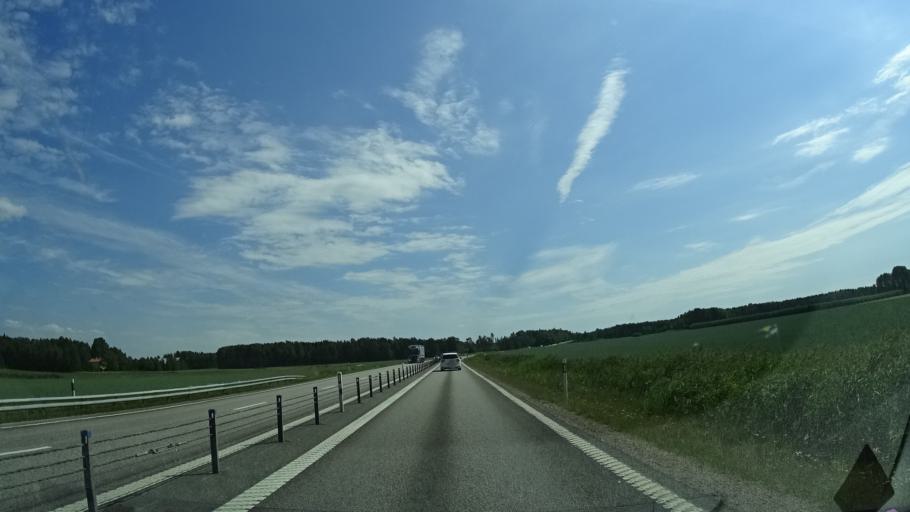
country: SE
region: Vaermland
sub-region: Kristinehamns Kommun
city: Kristinehamn
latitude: 59.3739
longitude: 13.9919
